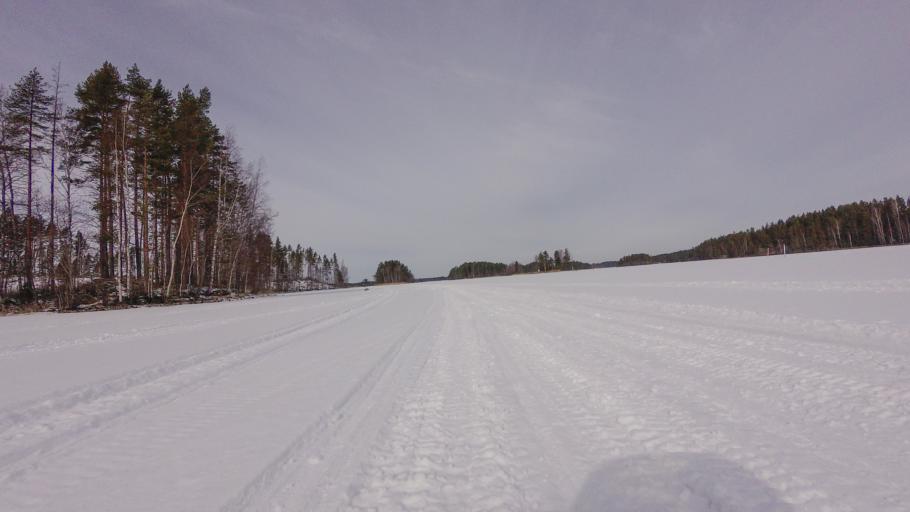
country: FI
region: Southern Savonia
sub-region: Savonlinna
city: Heinaevesi
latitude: 62.1218
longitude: 28.6202
